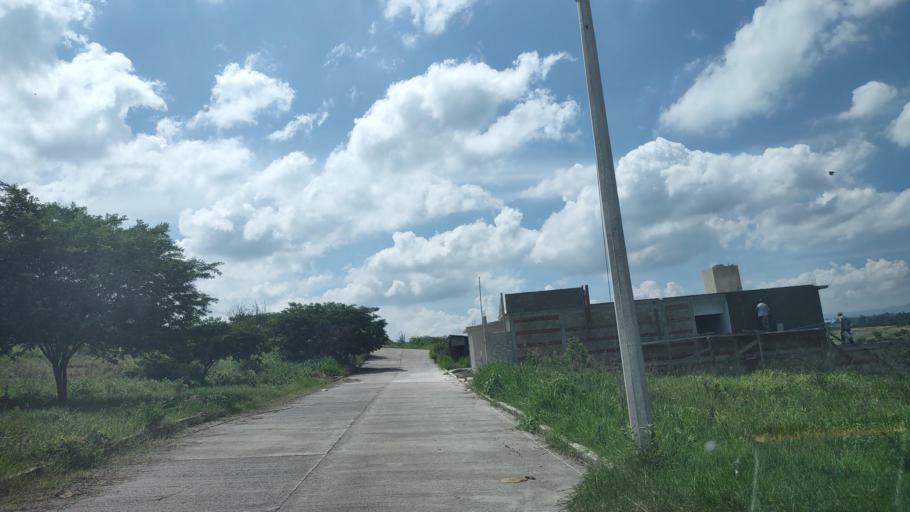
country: MX
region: Veracruz
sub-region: Emiliano Zapata
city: Dos Rios
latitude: 19.4942
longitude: -96.8169
